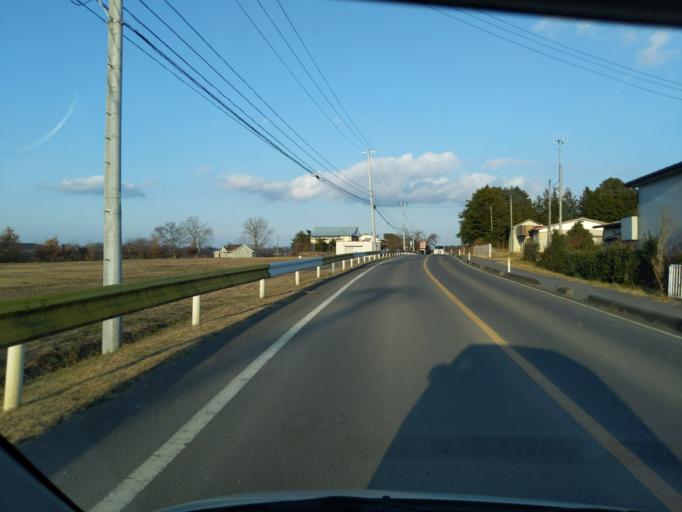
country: JP
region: Miyagi
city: Wakuya
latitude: 38.6870
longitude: 141.1321
